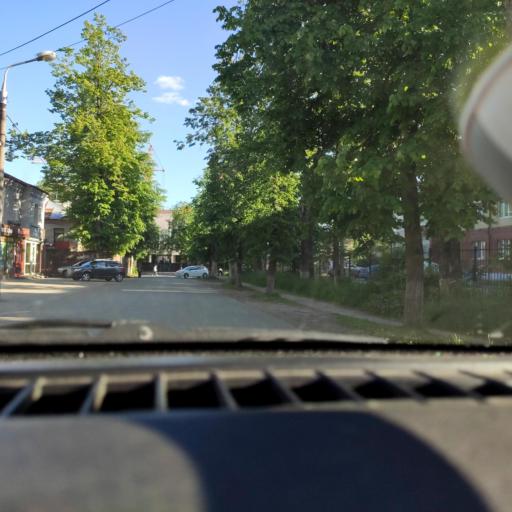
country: RU
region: Perm
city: Perm
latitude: 58.1126
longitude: 56.3094
